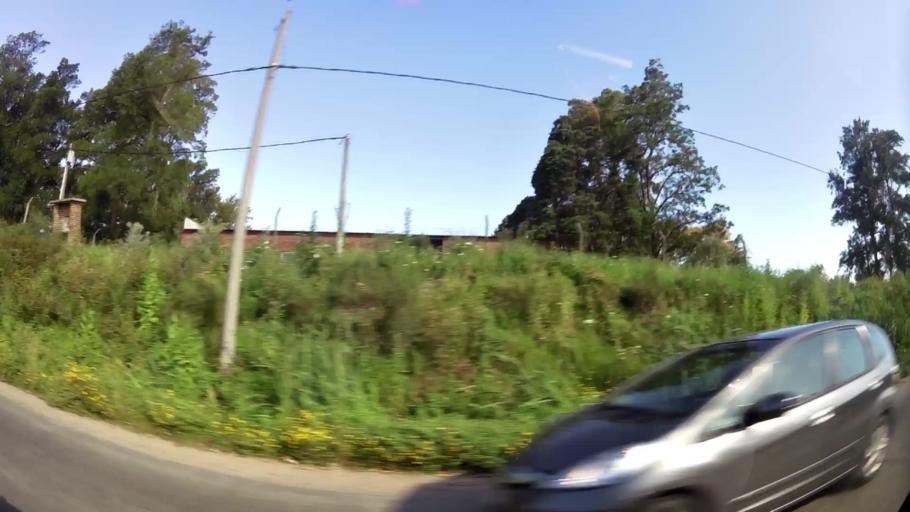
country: UY
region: Canelones
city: La Paz
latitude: -34.8204
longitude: -56.1762
